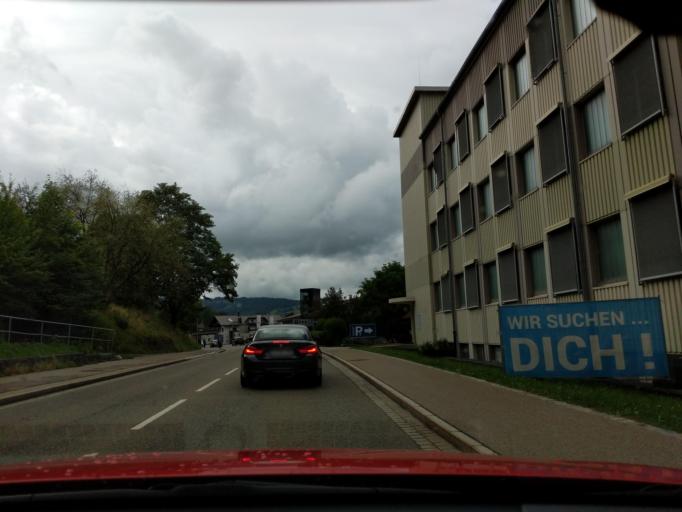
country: DE
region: Bavaria
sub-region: Swabia
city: Immenstadt im Allgau
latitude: 47.5627
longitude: 10.2025
